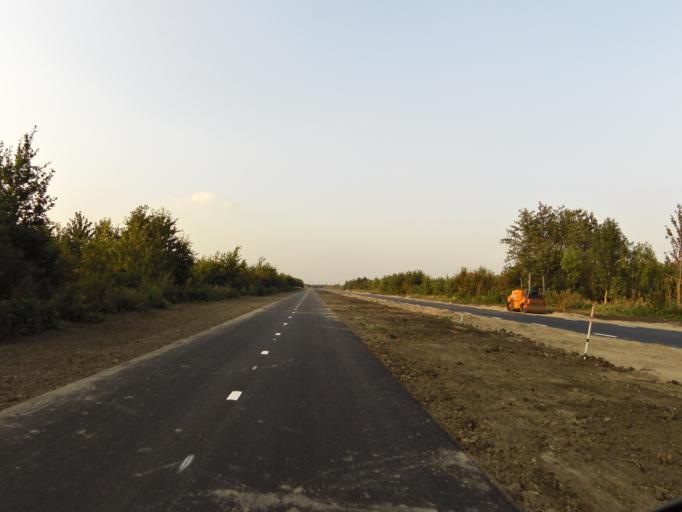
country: NL
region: South Holland
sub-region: Gemeente Rijnwoude
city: Benthuizen
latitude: 52.0667
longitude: 4.5638
